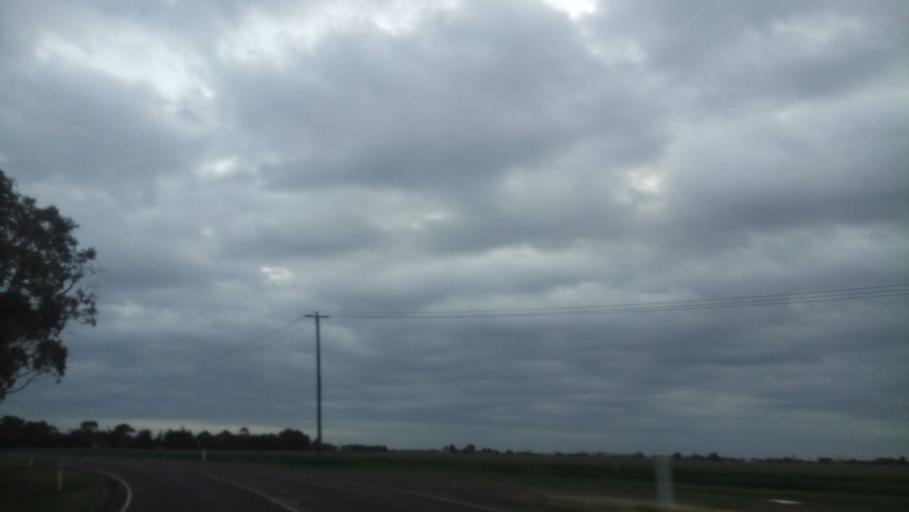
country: AU
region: Victoria
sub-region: Wyndham
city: Point Cook
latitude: -37.9234
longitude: 144.7435
